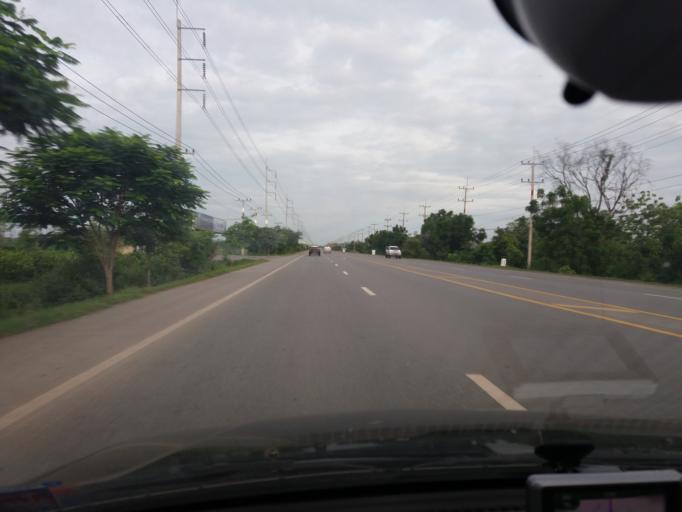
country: TH
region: Suphan Buri
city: U Thong
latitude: 14.3368
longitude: 99.8224
